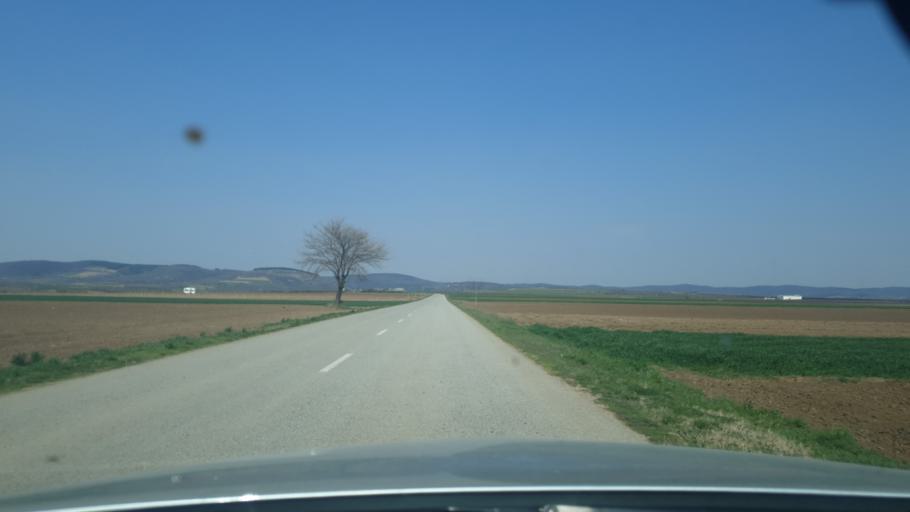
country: RS
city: Vrdnik
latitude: 45.0775
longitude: 19.7701
